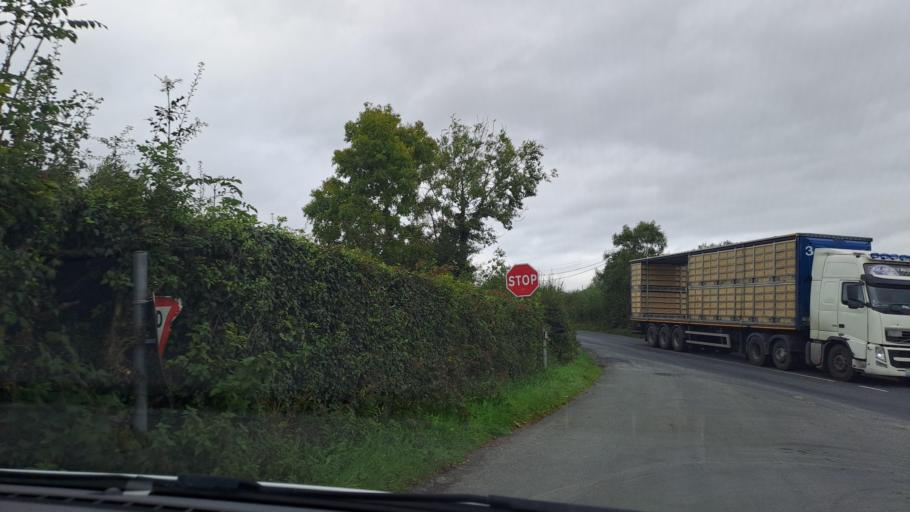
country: IE
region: Ulster
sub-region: An Cabhan
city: Bailieborough
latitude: 54.0160
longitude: -6.9315
